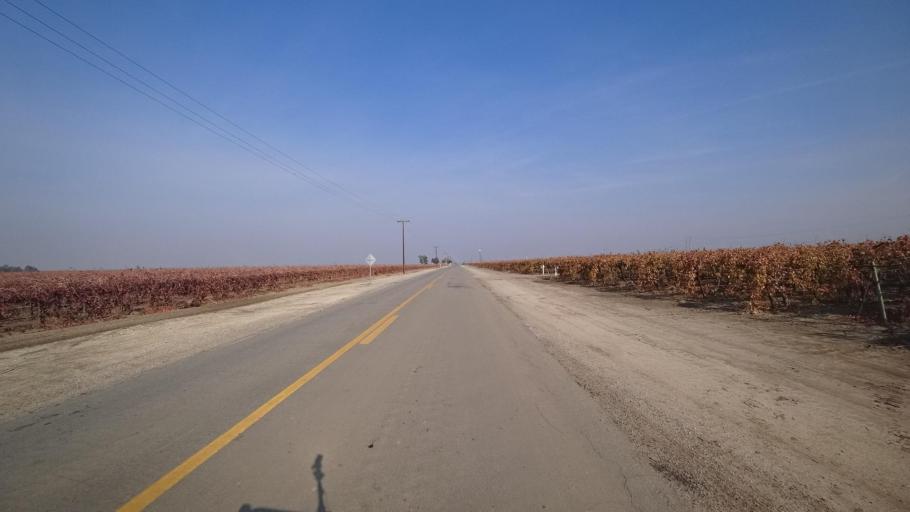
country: US
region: California
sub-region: Kern County
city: Arvin
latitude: 35.0413
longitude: -118.8466
